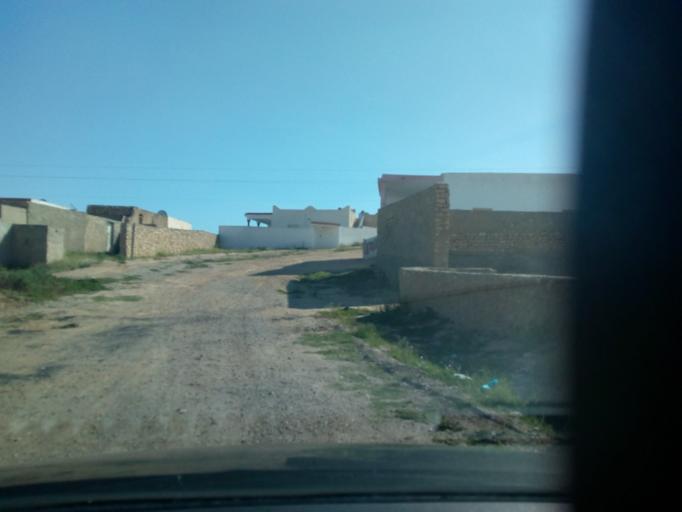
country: TN
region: Safaqis
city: Sfax
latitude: 34.7311
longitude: 10.6036
